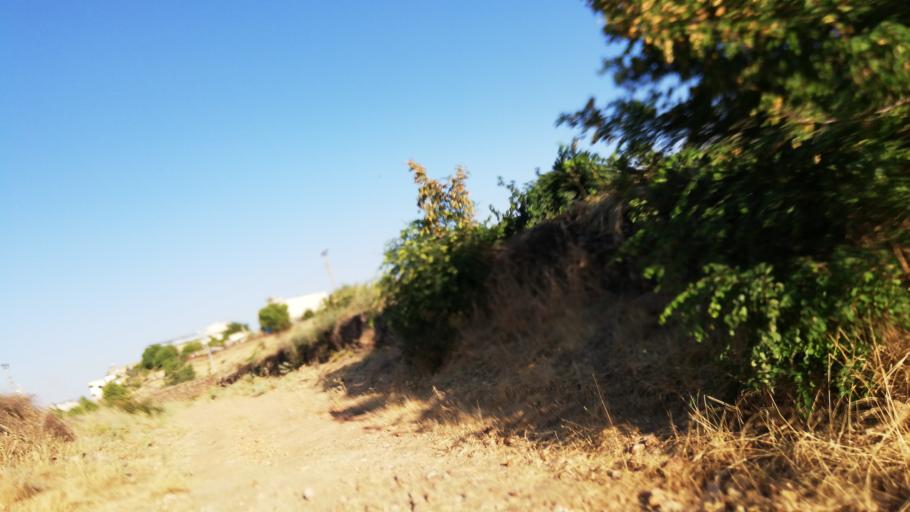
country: TR
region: Mardin
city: Kindirip
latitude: 37.4458
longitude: 41.2126
